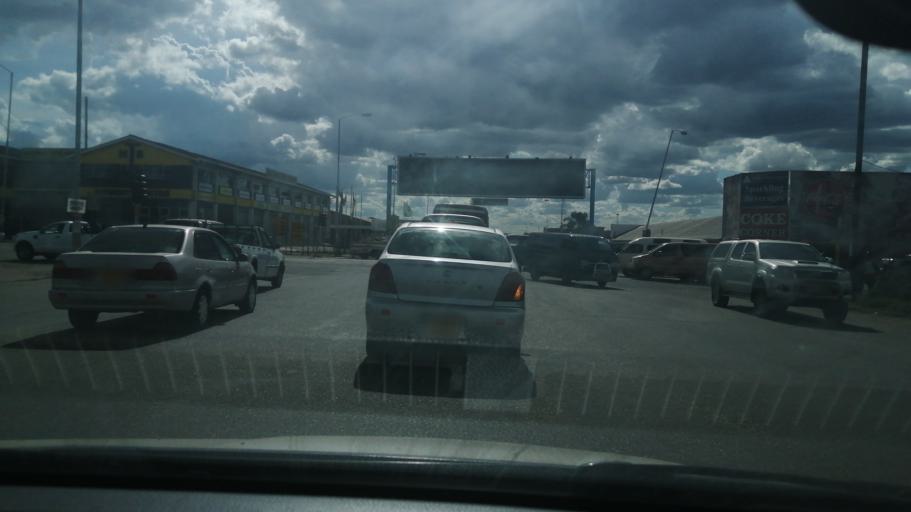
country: ZW
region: Harare
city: Harare
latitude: -17.8526
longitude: 31.0540
